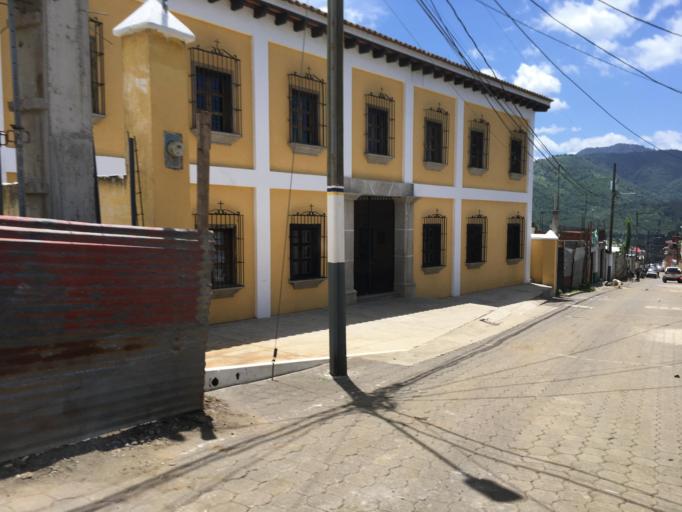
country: GT
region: Sacatepequez
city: Ciudad Vieja
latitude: 14.5239
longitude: -90.7497
